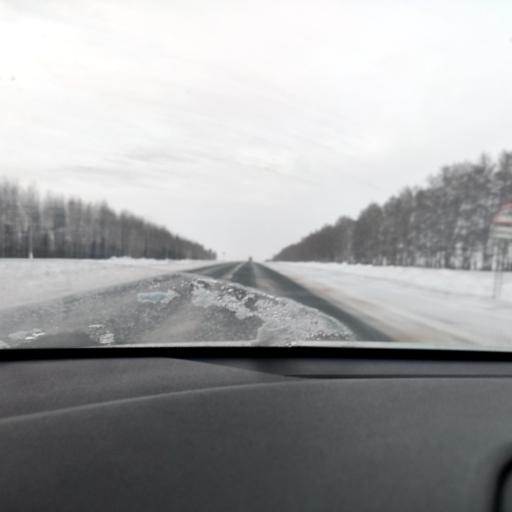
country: RU
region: Tatarstan
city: Sviyazhsk
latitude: 55.6417
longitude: 48.8116
